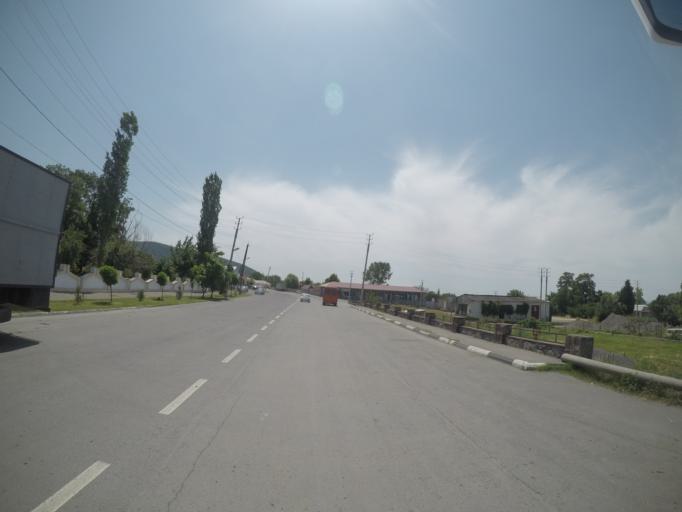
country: AZ
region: Qakh Rayon
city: Qax
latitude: 41.4163
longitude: 46.9066
